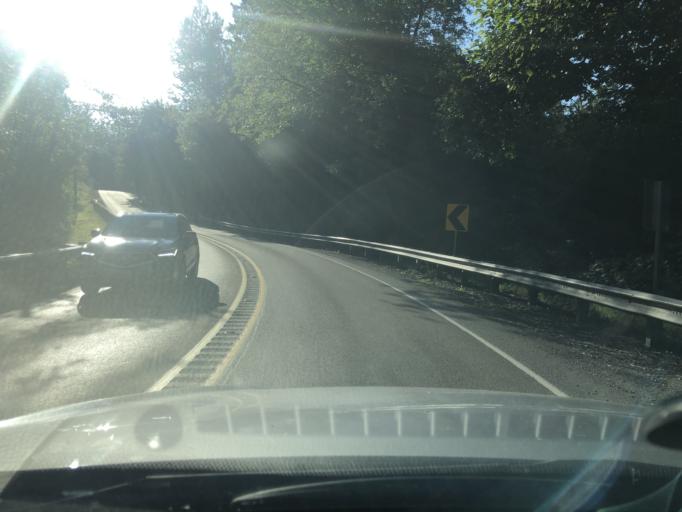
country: US
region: Washington
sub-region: Pierce County
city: Bonney Lake
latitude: 47.2483
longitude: -122.1714
